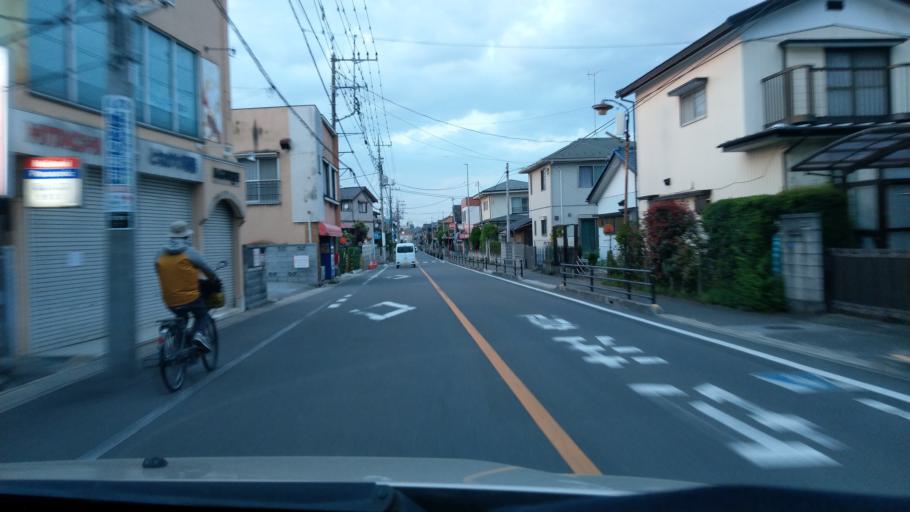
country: JP
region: Saitama
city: Iwatsuki
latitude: 35.9525
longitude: 139.6958
